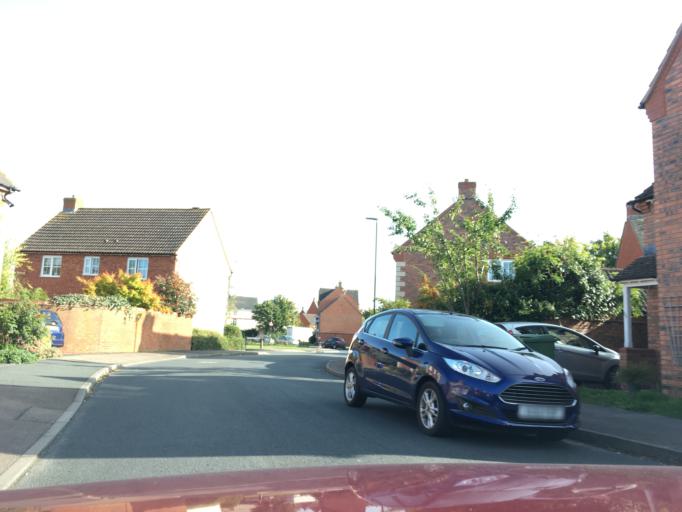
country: GB
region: England
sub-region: Gloucestershire
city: Tewkesbury
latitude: 51.9846
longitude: -2.1406
